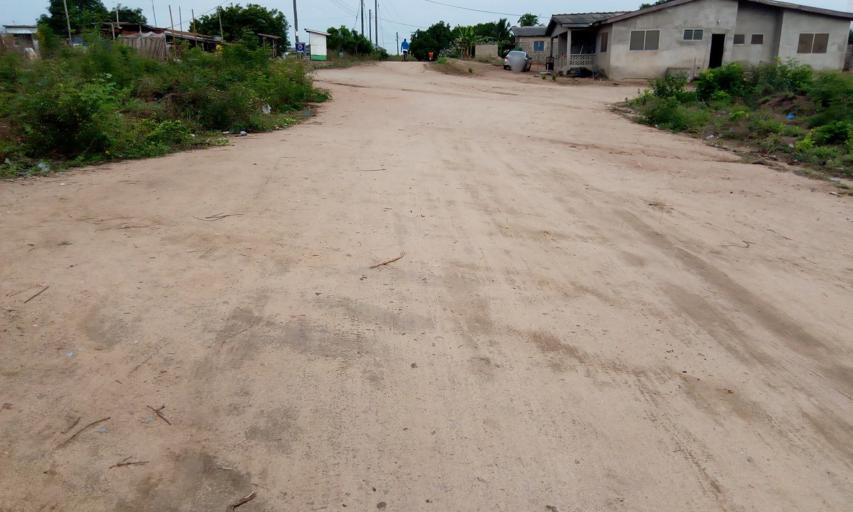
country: GH
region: Central
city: Winneba
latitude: 5.3577
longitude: -0.6201
